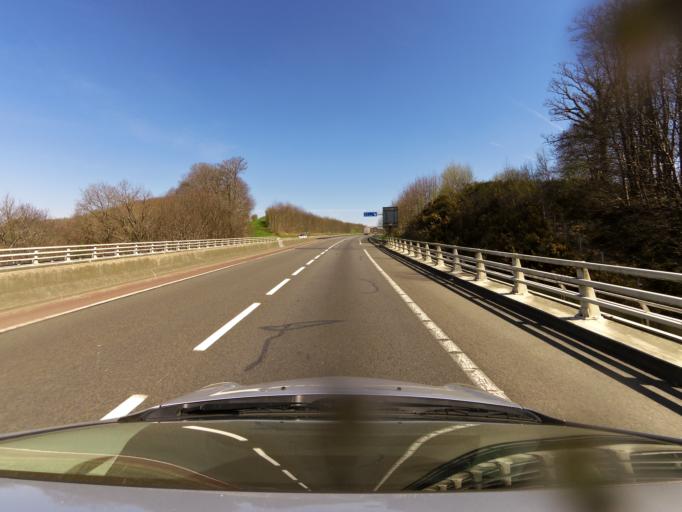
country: FR
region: Lower Normandy
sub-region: Departement de la Manche
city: Saint-Senier-sous-Avranches
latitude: 48.7384
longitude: -1.2931
